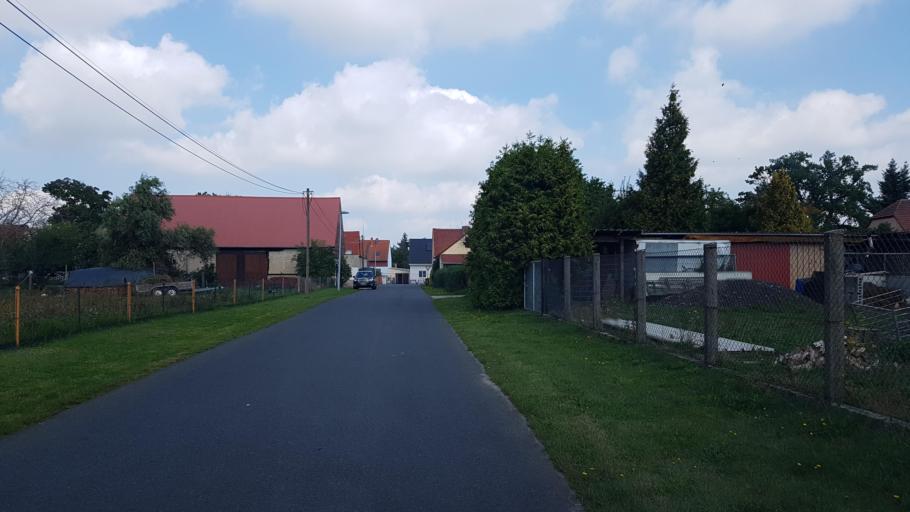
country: DE
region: Brandenburg
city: Drahnsdorf
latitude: 51.8163
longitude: 13.5981
